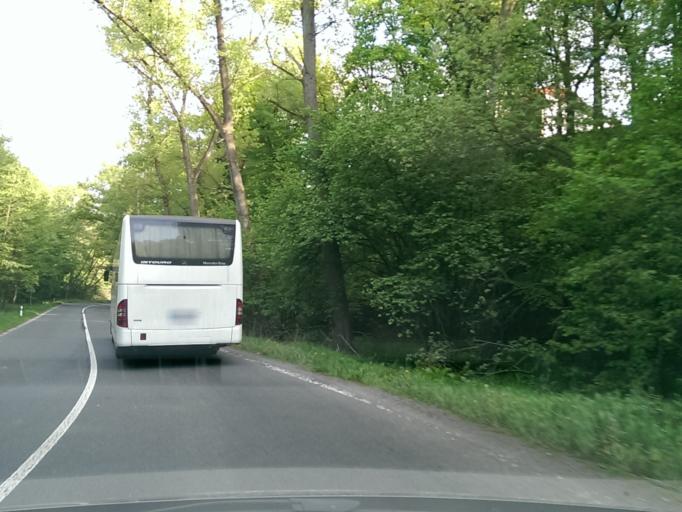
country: CZ
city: Duba
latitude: 50.5271
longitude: 14.5198
